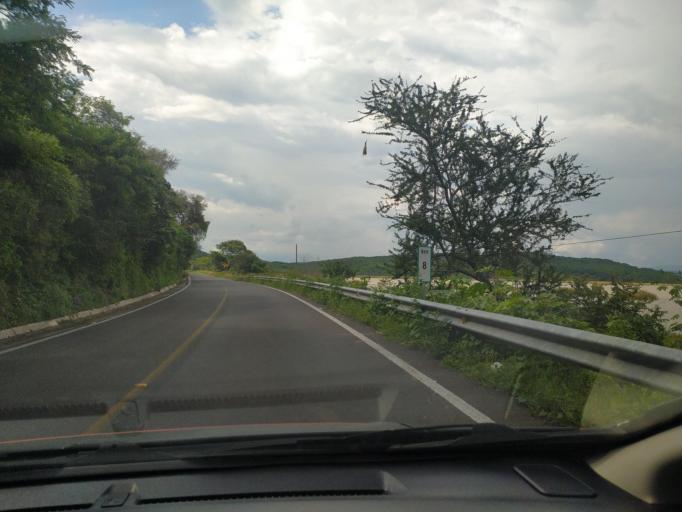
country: MX
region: Jalisco
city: Villa Corona
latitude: 20.3596
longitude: -103.6668
